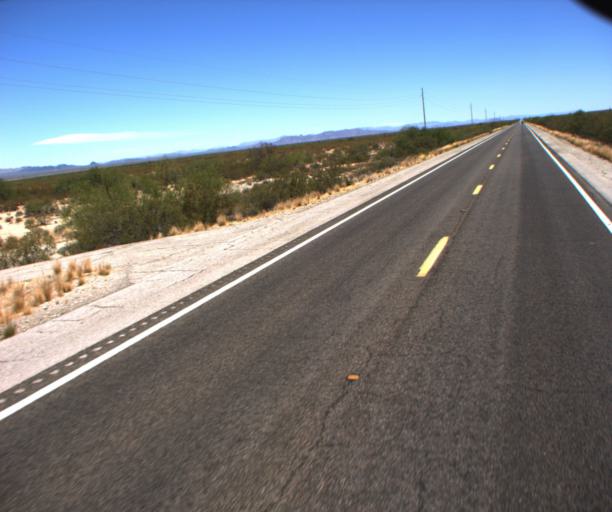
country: US
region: Arizona
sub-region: La Paz County
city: Salome
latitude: 33.8773
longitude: -113.3729
